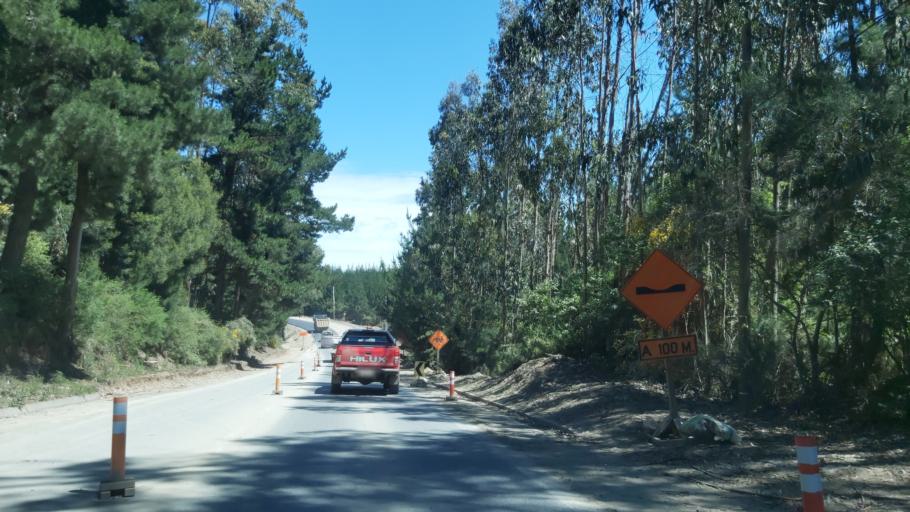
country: CL
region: Maule
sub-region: Provincia de Talca
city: Constitucion
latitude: -35.3764
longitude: -72.4216
